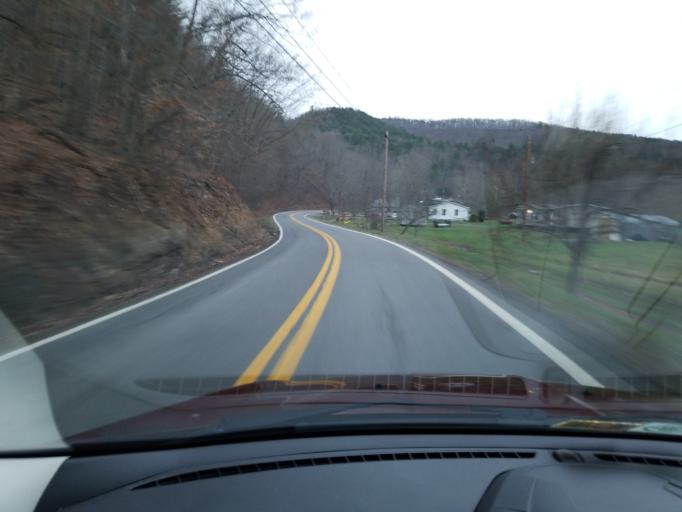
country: US
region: West Virginia
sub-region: Monroe County
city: Union
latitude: 37.5110
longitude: -80.6115
